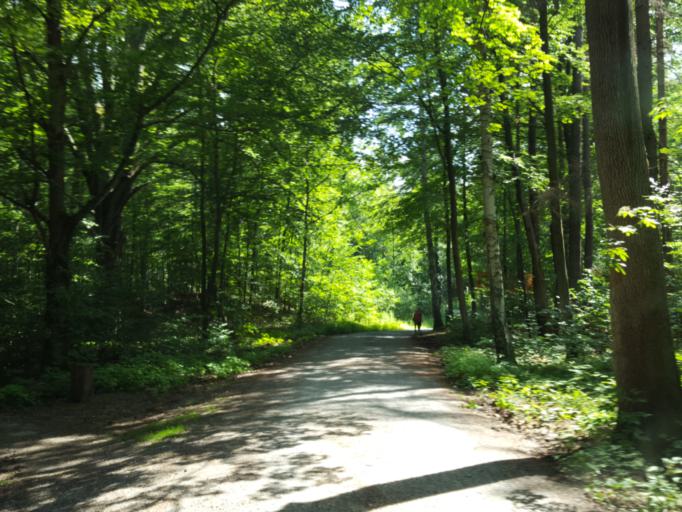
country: DE
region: Saxony
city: Albertstadt
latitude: 51.1138
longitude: 13.7928
